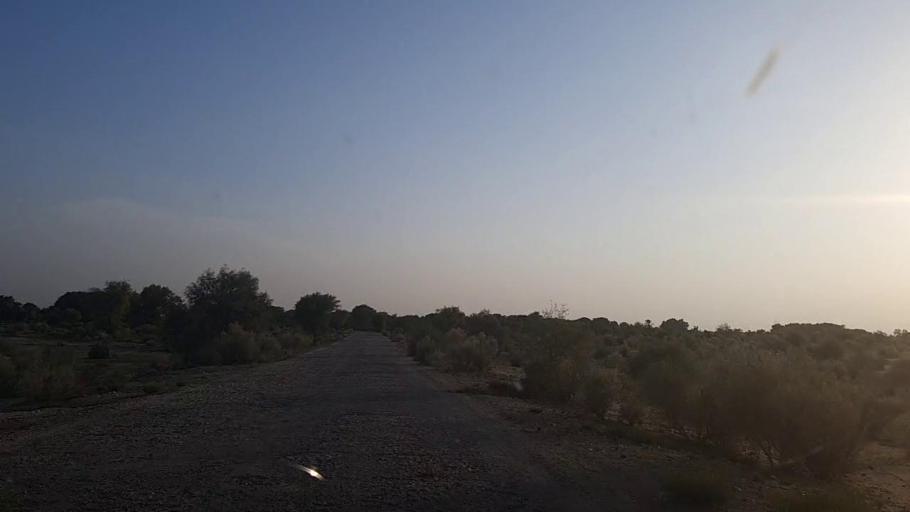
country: PK
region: Sindh
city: Khanpur
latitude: 27.6373
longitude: 69.4503
